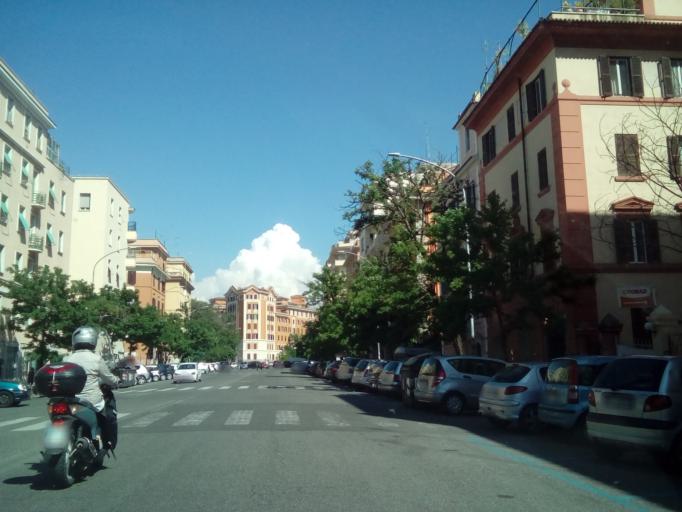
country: IT
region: Latium
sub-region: Citta metropolitana di Roma Capitale
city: Rome
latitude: 41.8838
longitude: 12.5181
